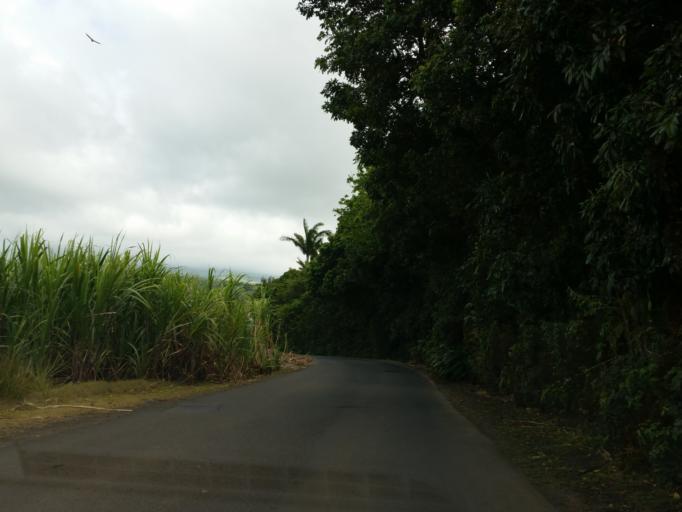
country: RE
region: Reunion
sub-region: Reunion
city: Sainte-Suzanne
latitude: -20.9159
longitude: 55.6152
